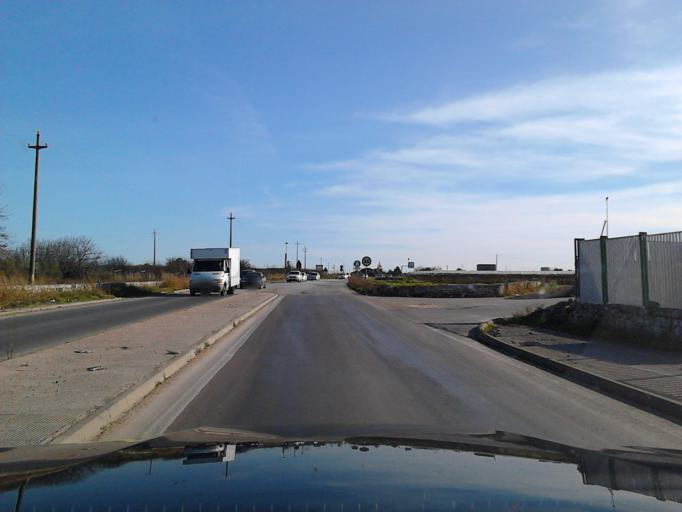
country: IT
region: Apulia
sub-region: Provincia di Bari
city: Noicattaro
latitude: 41.0228
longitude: 16.9722
